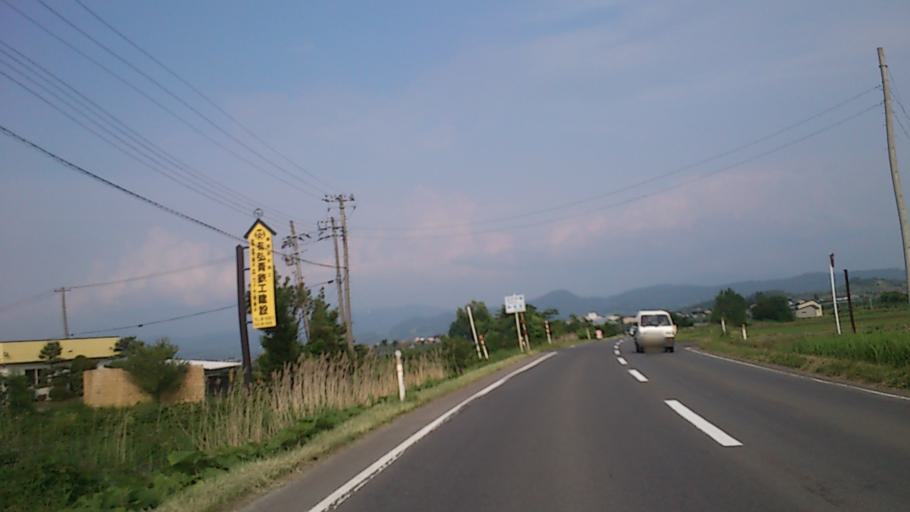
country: JP
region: Aomori
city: Hirosaki
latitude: 40.5583
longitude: 140.5033
